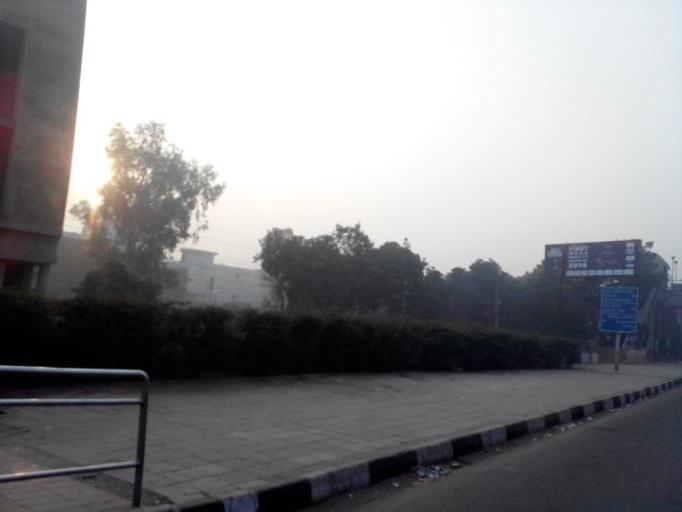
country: IN
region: Uttar Pradesh
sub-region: Gautam Buddha Nagar
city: Noida
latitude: 28.6611
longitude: 77.3202
